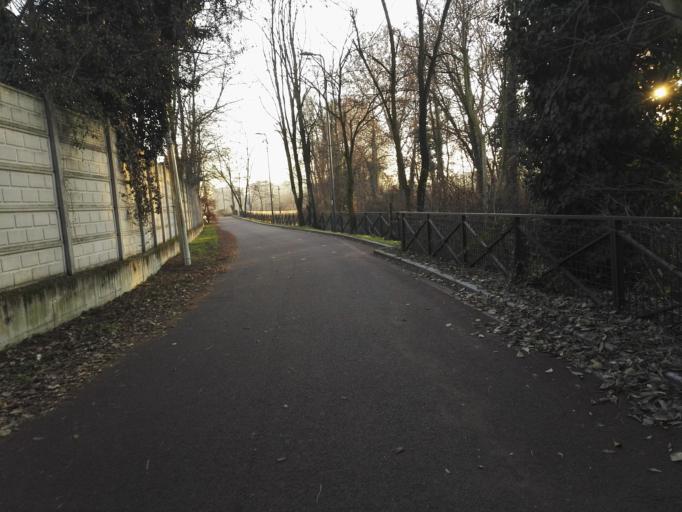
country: IT
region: Lombardy
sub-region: Citta metropolitana di Milano
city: Cologno Monzese
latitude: 45.5174
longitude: 9.2567
